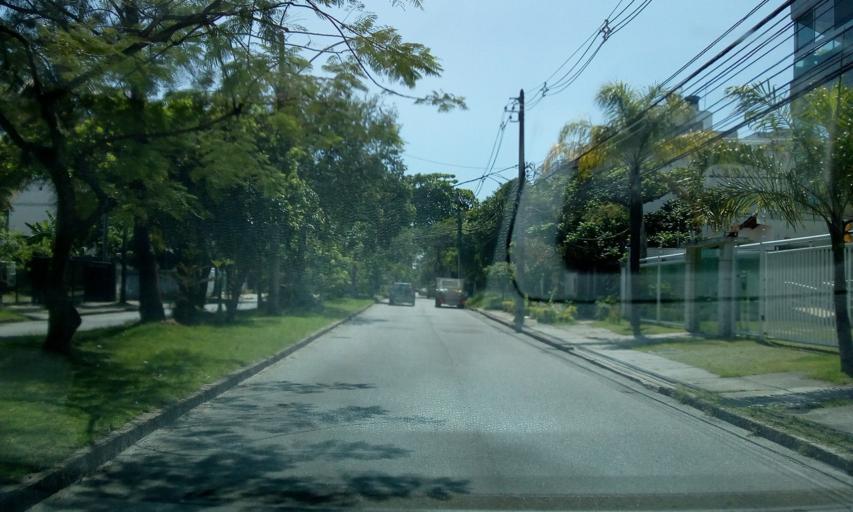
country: BR
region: Rio de Janeiro
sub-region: Nilopolis
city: Nilopolis
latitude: -23.0208
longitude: -43.4757
